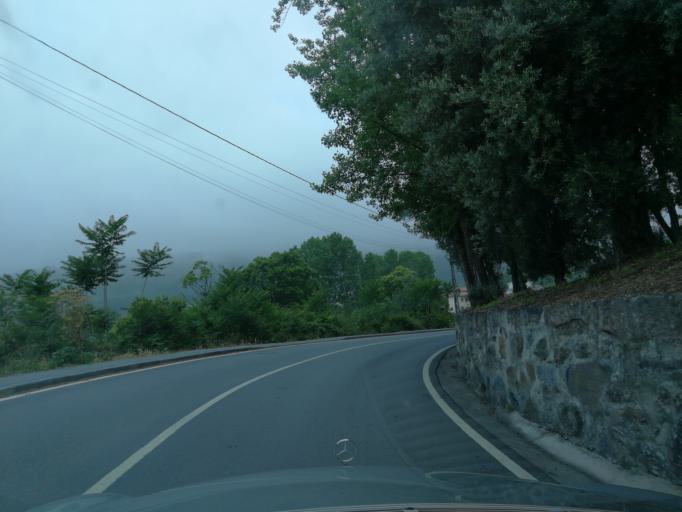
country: PT
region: Braga
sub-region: Guimaraes
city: Ponte
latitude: 41.5195
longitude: -8.3599
